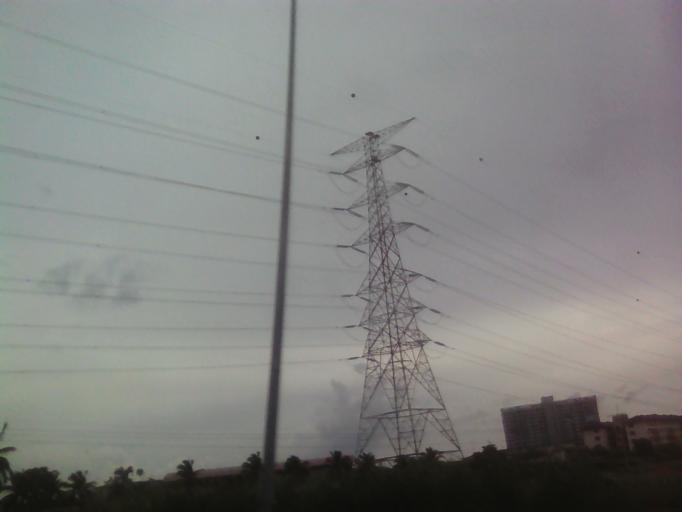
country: MY
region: Penang
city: Perai
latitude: 5.4001
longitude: 100.4028
